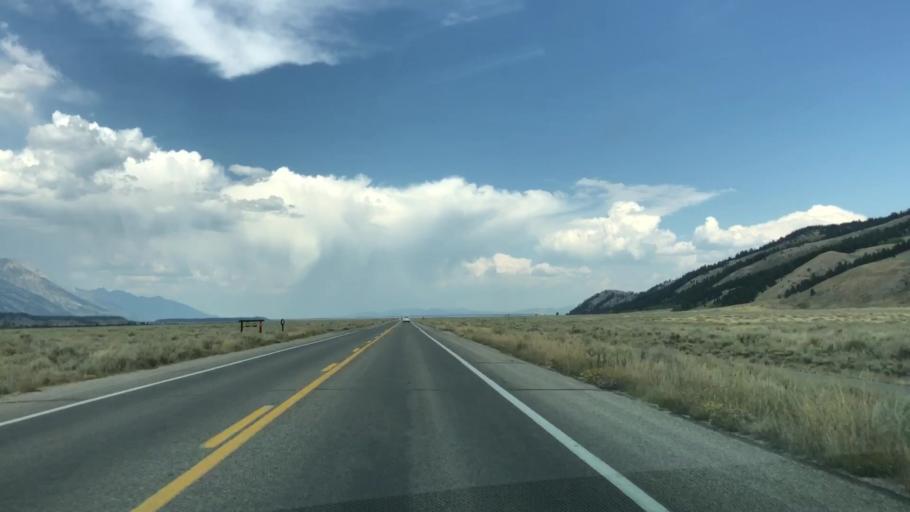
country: US
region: Wyoming
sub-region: Teton County
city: Jackson
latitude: 43.6240
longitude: -110.7199
